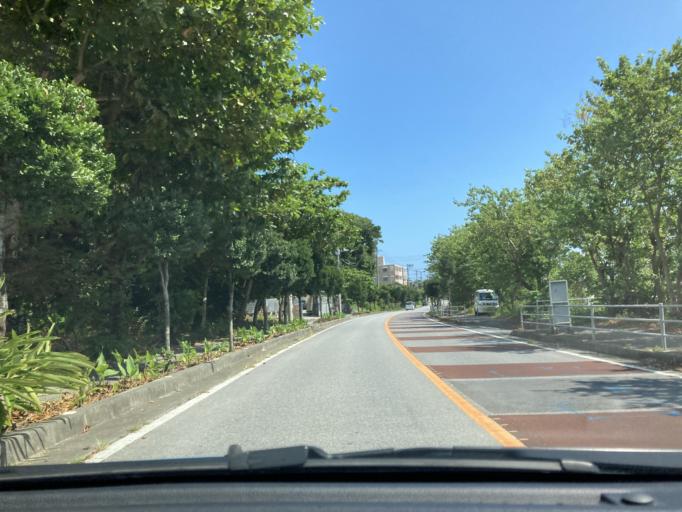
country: JP
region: Okinawa
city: Ginowan
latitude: 26.1815
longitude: 127.7699
